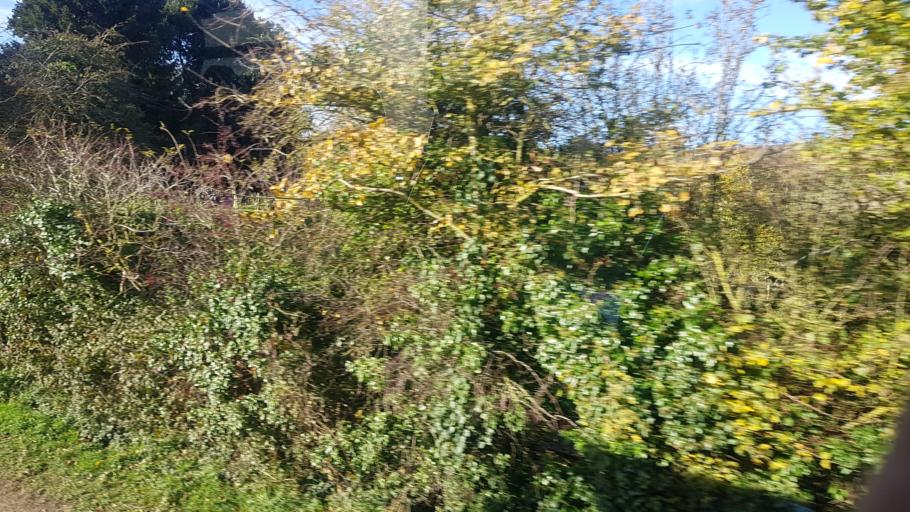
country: GB
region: England
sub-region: Isle of Wight
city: Newport
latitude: 50.6635
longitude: -1.3473
